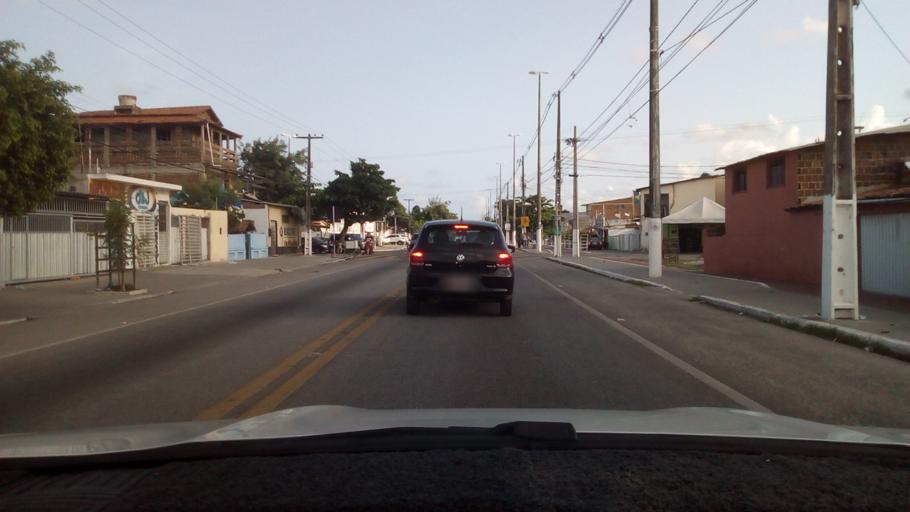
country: BR
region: Paraiba
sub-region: Cabedelo
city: Cabedelo
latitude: -6.9778
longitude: -34.8310
